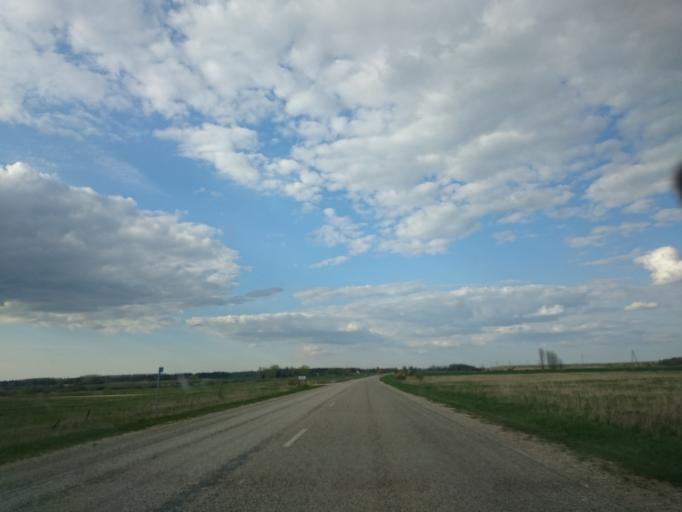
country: LV
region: Aizpute
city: Aizpute
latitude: 56.7467
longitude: 21.6113
